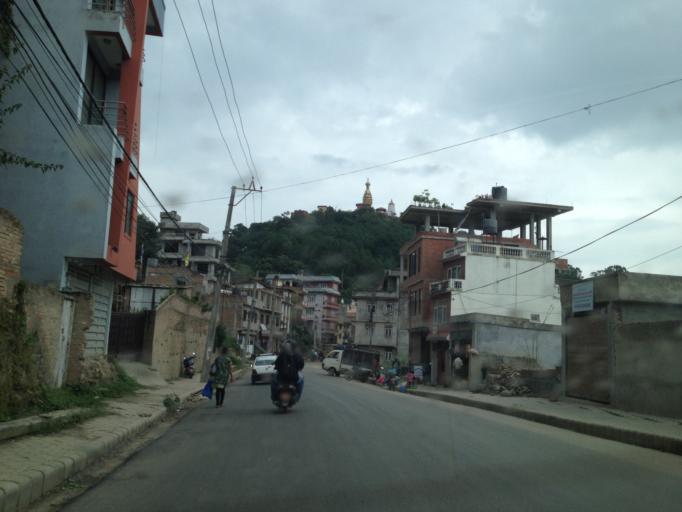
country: NP
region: Central Region
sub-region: Bagmati Zone
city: Kathmandu
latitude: 27.7112
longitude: 85.2896
